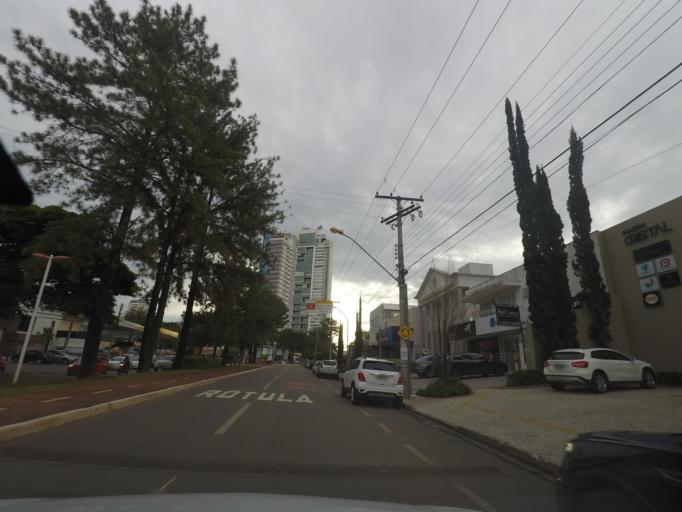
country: BR
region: Goias
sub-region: Goiania
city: Goiania
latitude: -16.7040
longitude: -49.2598
